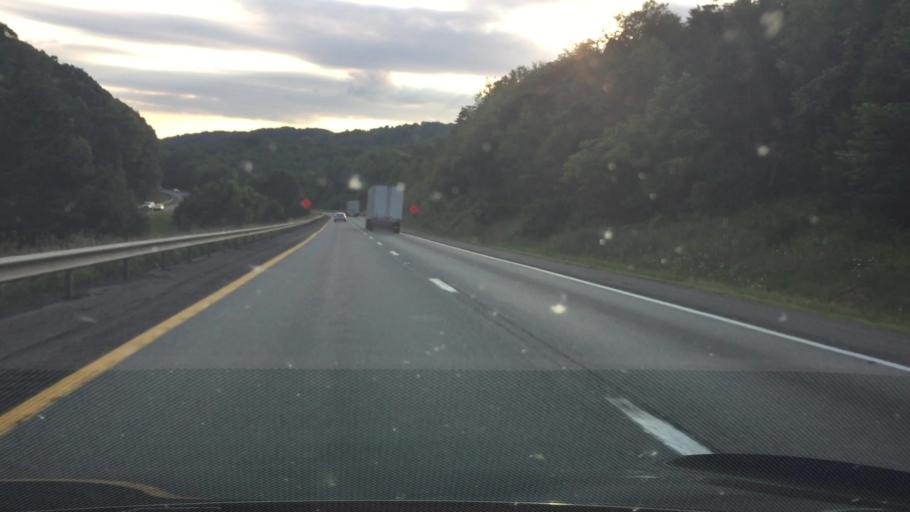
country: US
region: Virginia
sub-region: City of Radford
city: Radford
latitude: 37.1008
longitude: -80.5487
